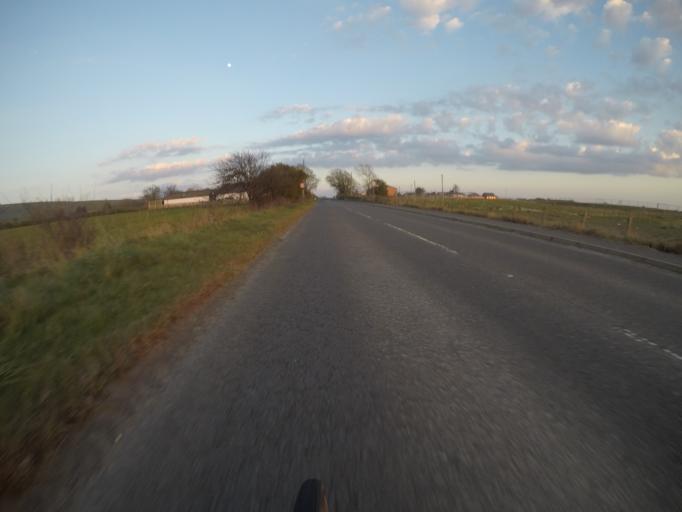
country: GB
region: Scotland
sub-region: South Ayrshire
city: Troon
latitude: 55.5605
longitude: -4.6315
